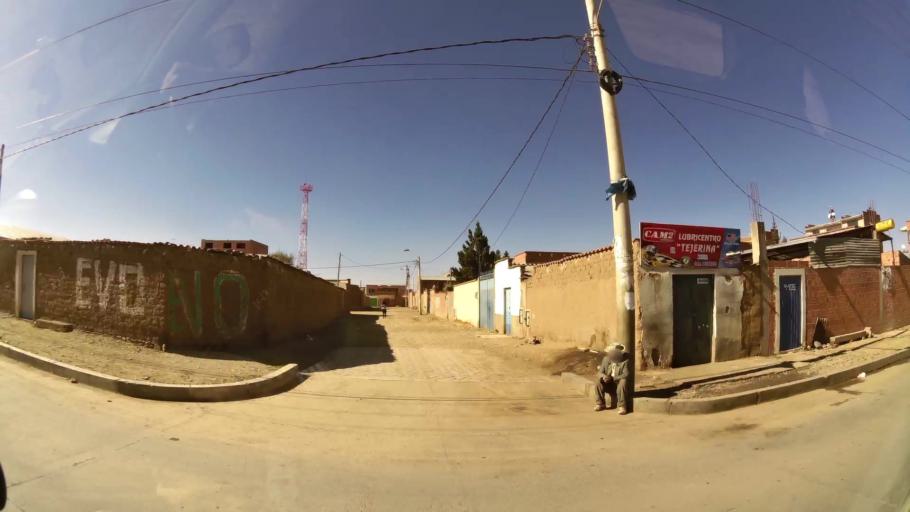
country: BO
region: La Paz
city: La Paz
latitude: -16.5324
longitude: -68.2133
